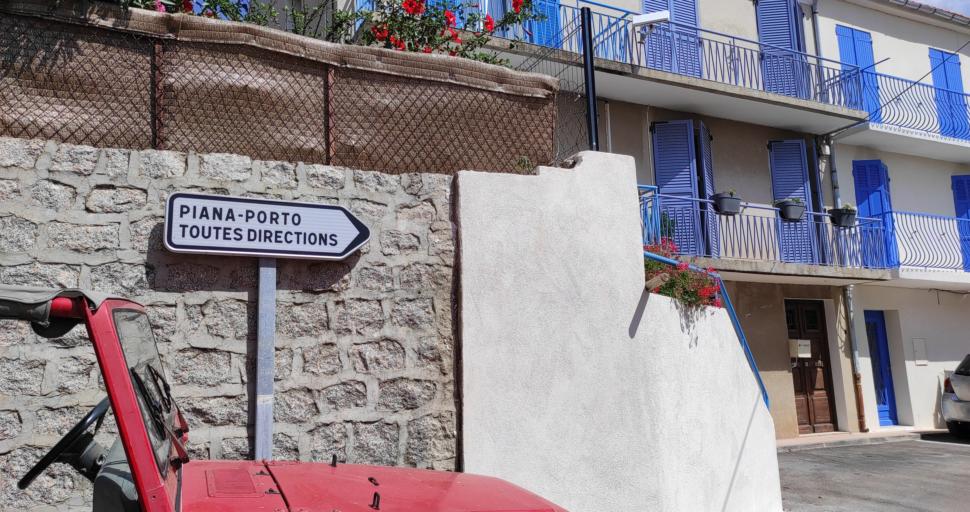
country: FR
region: Corsica
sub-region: Departement de la Corse-du-Sud
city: Cargese
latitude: 42.1345
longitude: 8.5941
